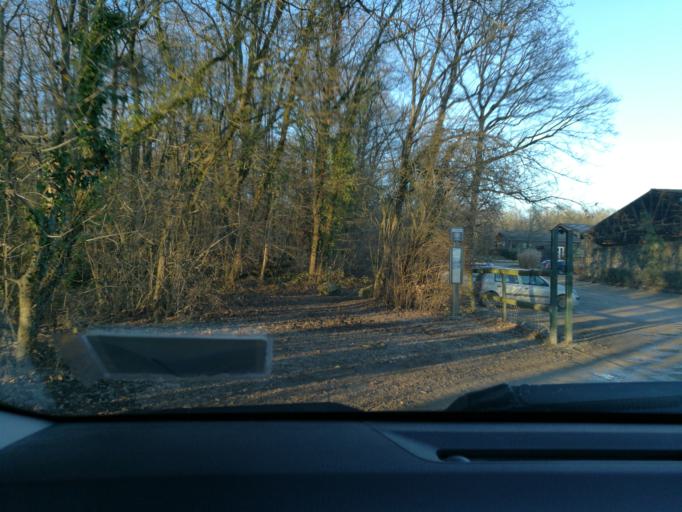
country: FR
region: Centre
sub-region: Departement du Loiret
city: Semoy
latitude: 47.9376
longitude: 1.9708
